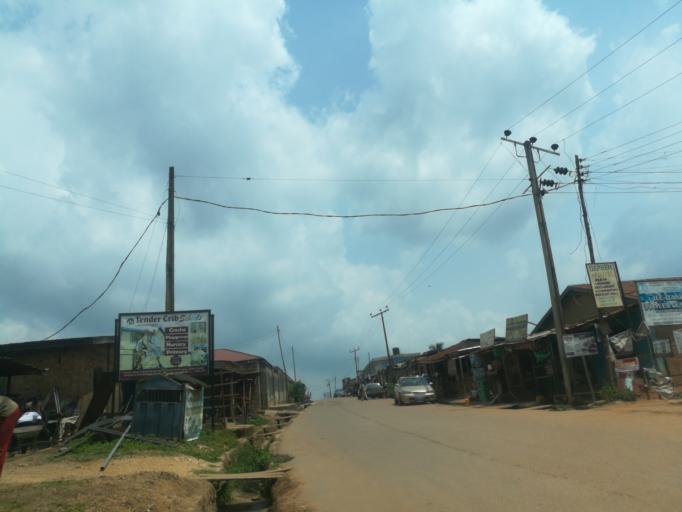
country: NG
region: Oyo
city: Moniya
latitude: 7.4524
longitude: 3.9565
